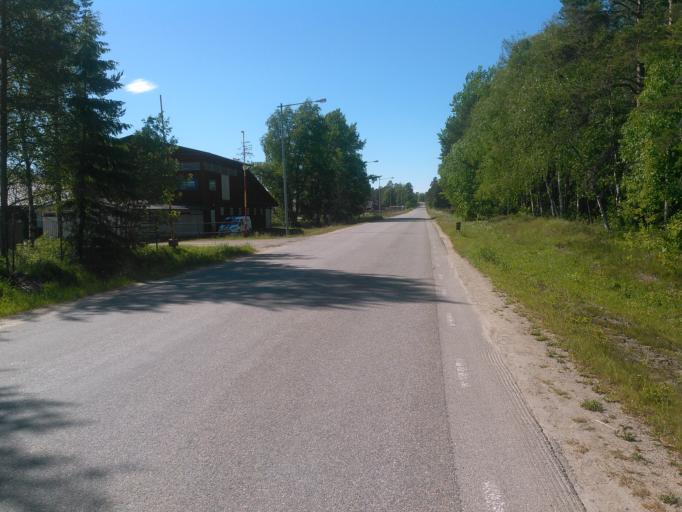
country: SE
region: Vaesterbotten
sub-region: Umea Kommun
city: Roback
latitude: 63.8225
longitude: 20.1865
